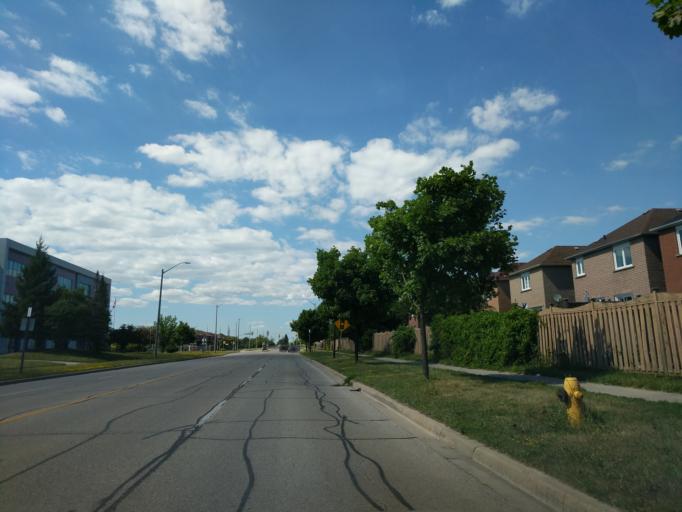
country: CA
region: Ontario
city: Markham
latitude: 43.8464
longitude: -79.2662
